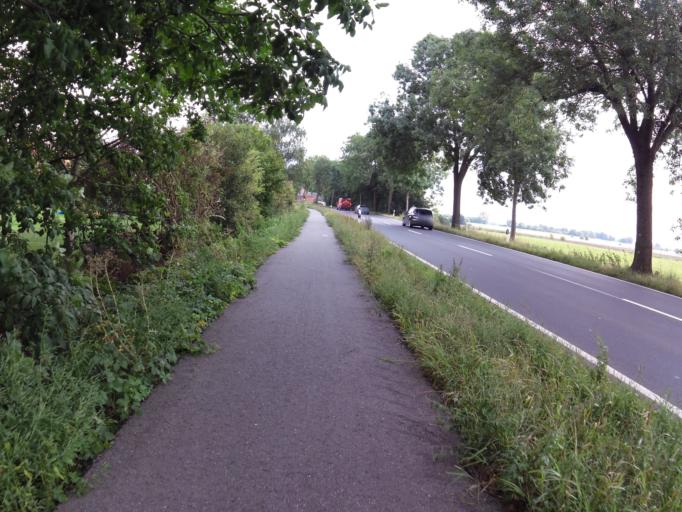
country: DE
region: Lower Saxony
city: Verden
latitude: 52.9224
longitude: 9.1885
